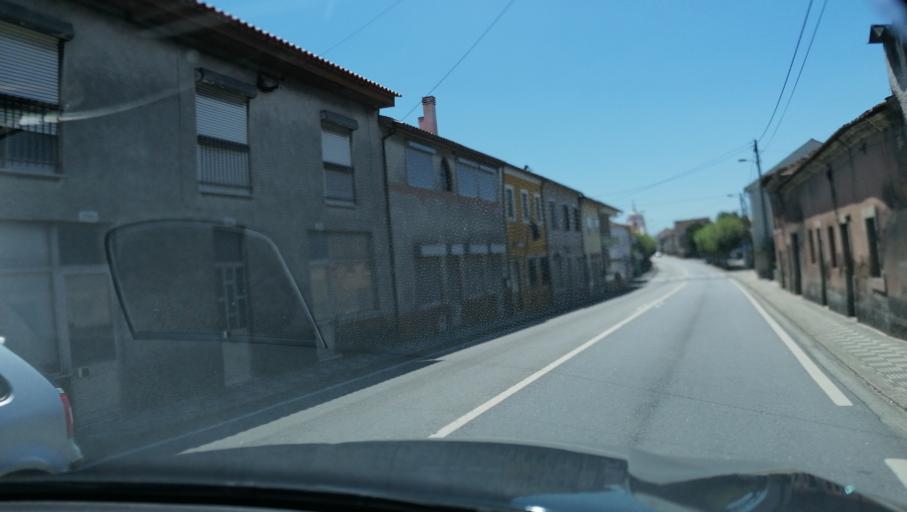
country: PT
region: Aveiro
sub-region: Anadia
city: Sangalhos
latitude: 40.4792
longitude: -8.4537
